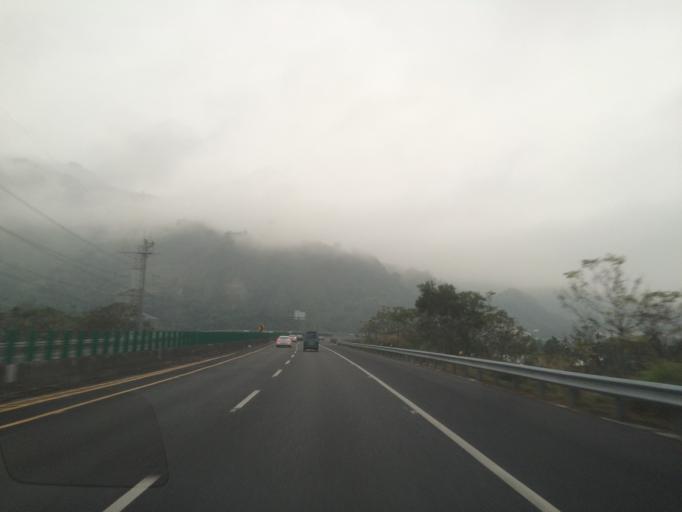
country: TW
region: Taiwan
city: Zhongxing New Village
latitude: 23.9949
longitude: 120.8011
